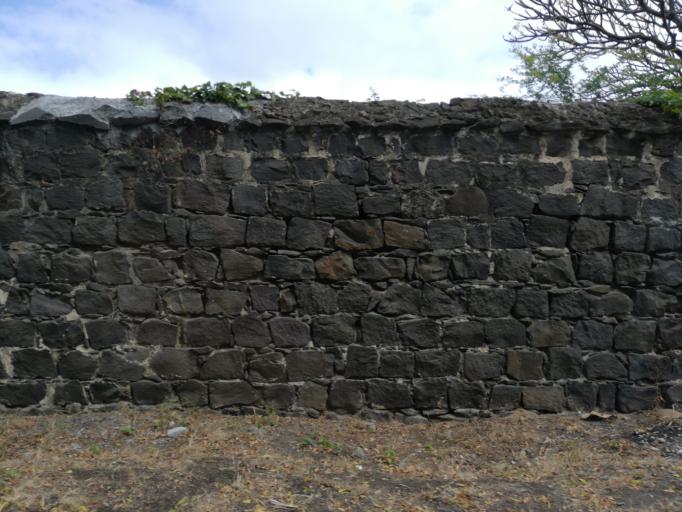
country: MU
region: Port Louis
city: Port Louis
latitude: -20.1580
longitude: 57.4859
